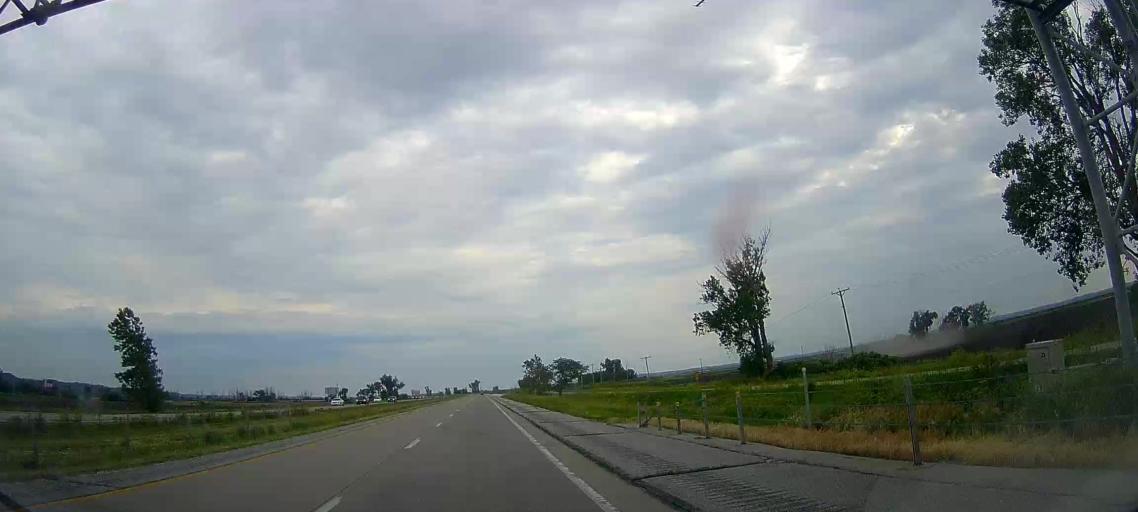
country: US
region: Iowa
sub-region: Harrison County
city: Missouri Valley
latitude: 41.5240
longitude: -95.9181
